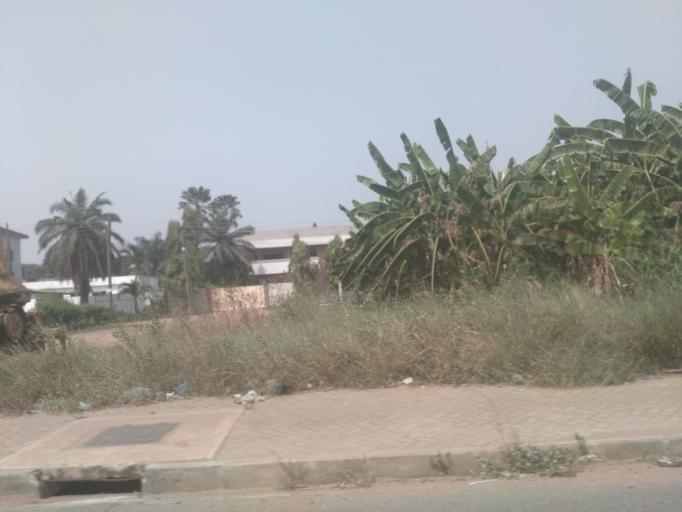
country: GH
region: Greater Accra
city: Dome
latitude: 5.6171
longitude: -0.1985
